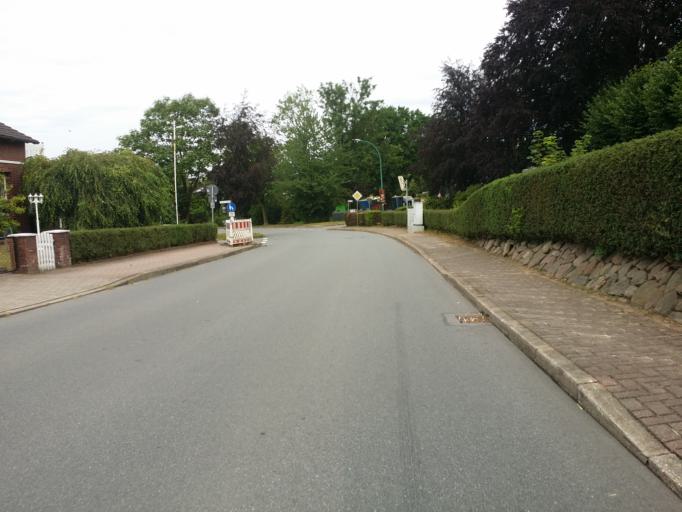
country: DE
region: Schleswig-Holstein
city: Oldendorf
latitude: 53.9529
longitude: 9.4589
